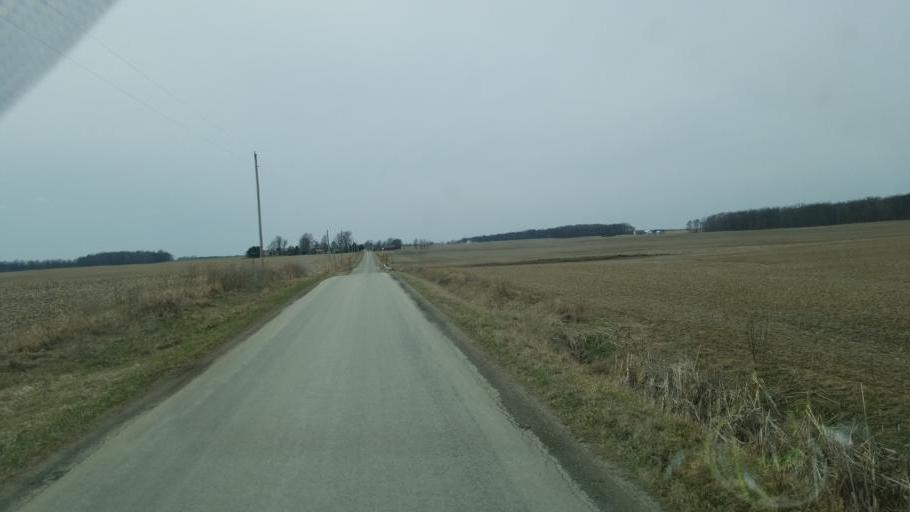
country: US
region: Ohio
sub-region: Huron County
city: Greenwich
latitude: 41.1444
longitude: -82.4993
